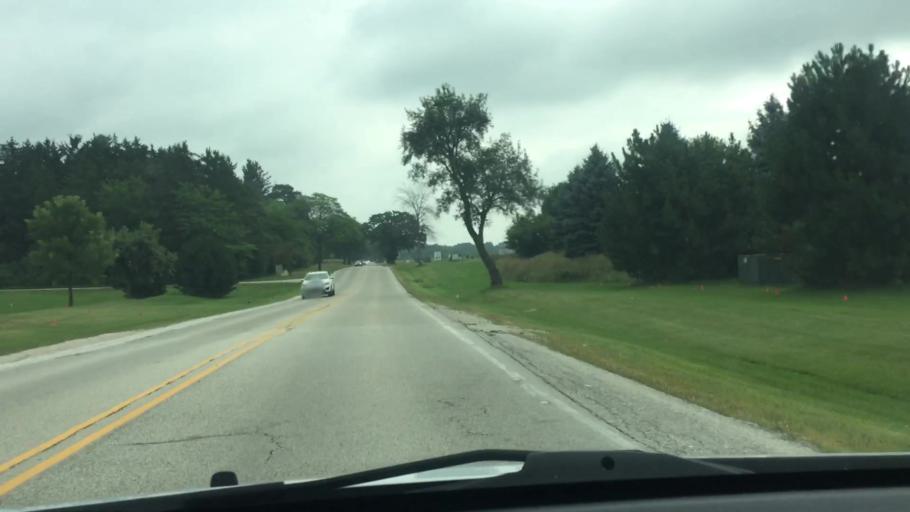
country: US
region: Wisconsin
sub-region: Waukesha County
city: Okauchee Lake
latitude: 43.0774
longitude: -88.4535
